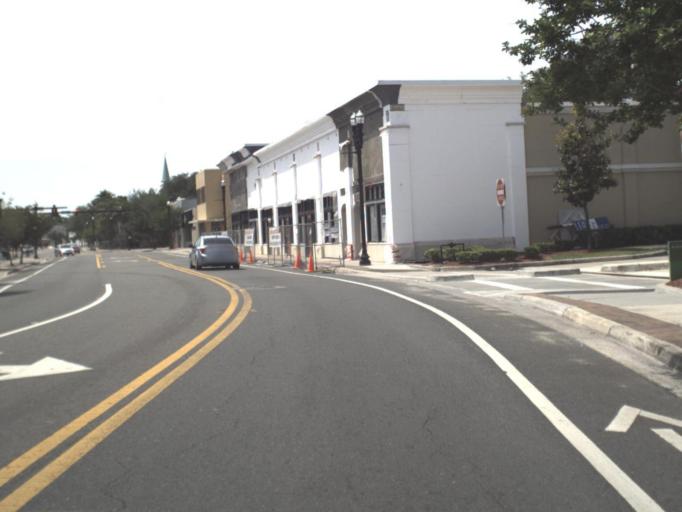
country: US
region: Florida
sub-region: Duval County
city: Jacksonville
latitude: 30.3087
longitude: -81.6547
